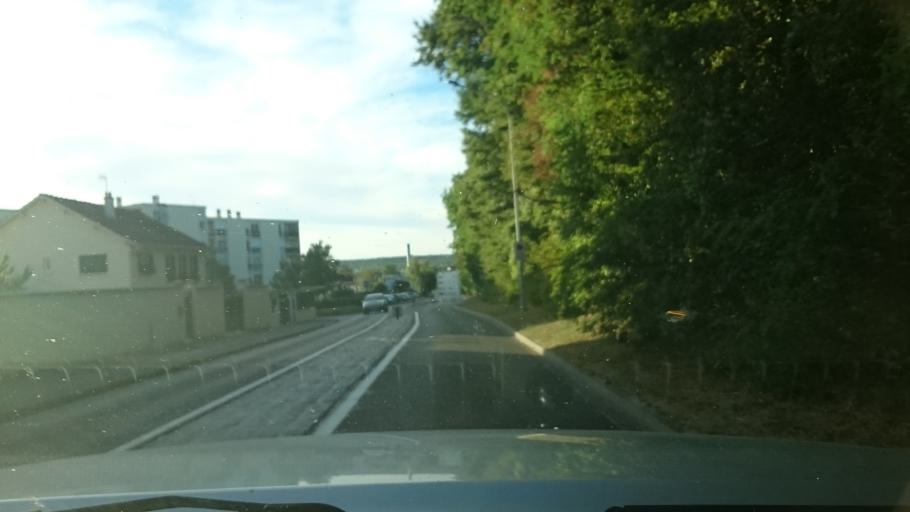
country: FR
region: Ile-de-France
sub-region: Departement de Seine-et-Marne
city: Samoreau
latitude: 48.4126
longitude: 2.7426
